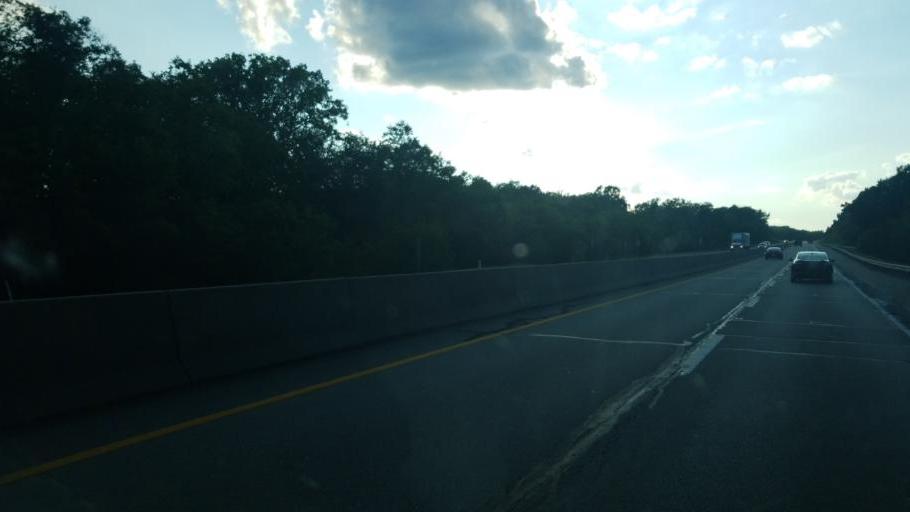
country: US
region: Pennsylvania
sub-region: Butler County
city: Fernway
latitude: 40.7210
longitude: -80.1466
